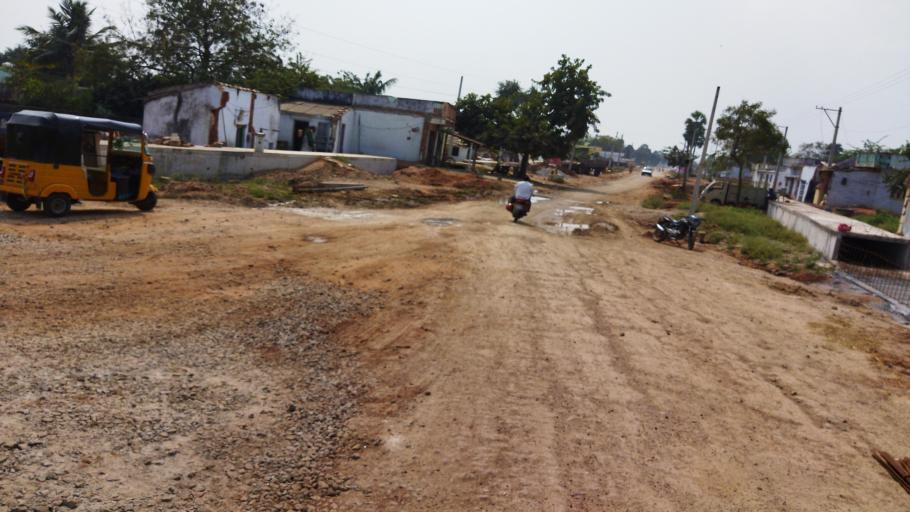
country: IN
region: Telangana
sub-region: Nalgonda
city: Nalgonda
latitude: 17.1242
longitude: 79.3674
